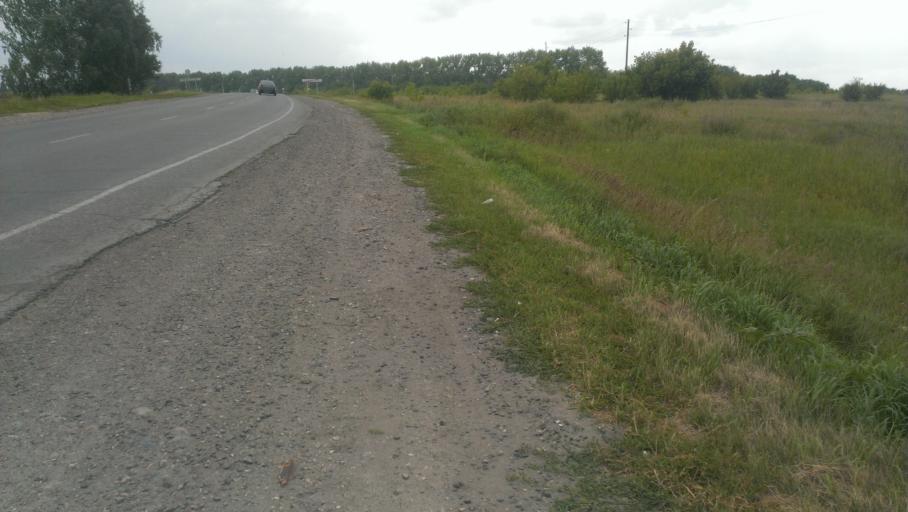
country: RU
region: Altai Krai
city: Gon'ba
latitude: 53.3902
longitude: 83.6009
